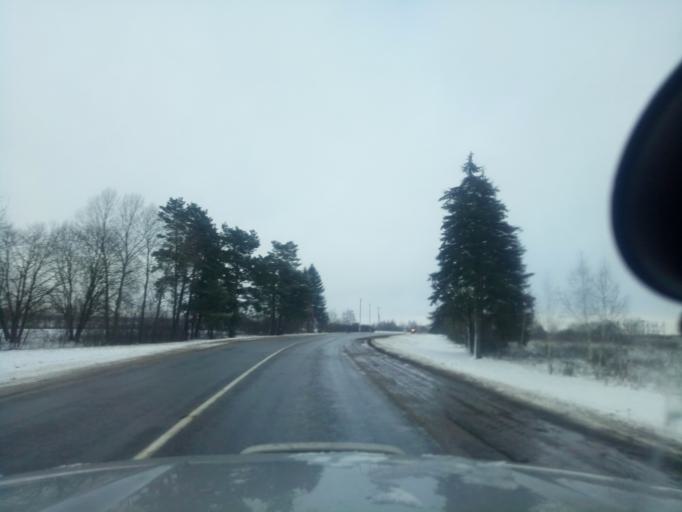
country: BY
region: Minsk
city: Tsimkavichy
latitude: 53.0983
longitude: 27.0436
